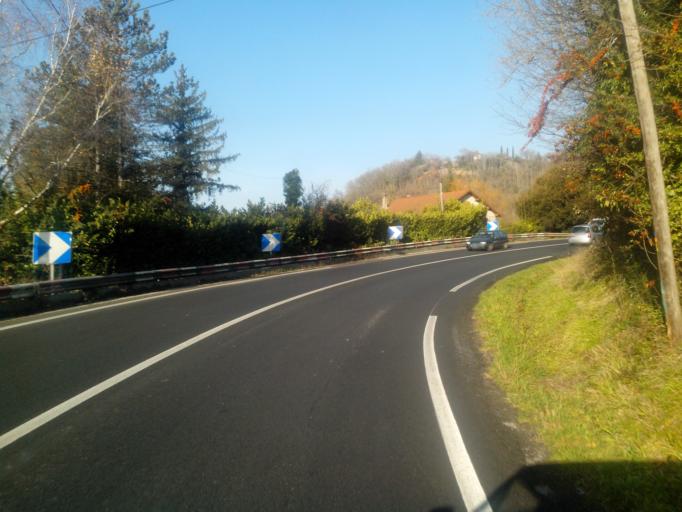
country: FR
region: Midi-Pyrenees
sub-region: Departement de l'Aveyron
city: Capdenac-Gare
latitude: 44.5820
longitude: 2.0661
